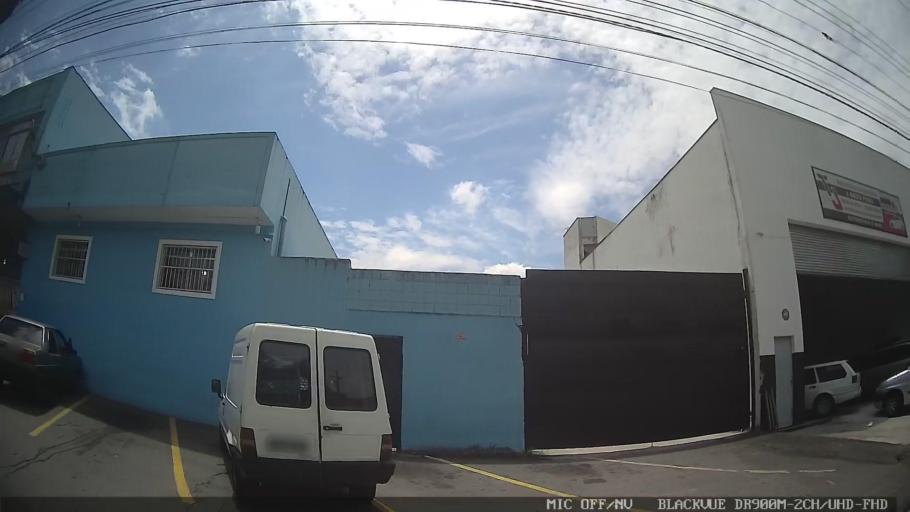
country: BR
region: Sao Paulo
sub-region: Ribeirao Pires
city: Ribeirao Pires
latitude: -23.7157
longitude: -46.4209
